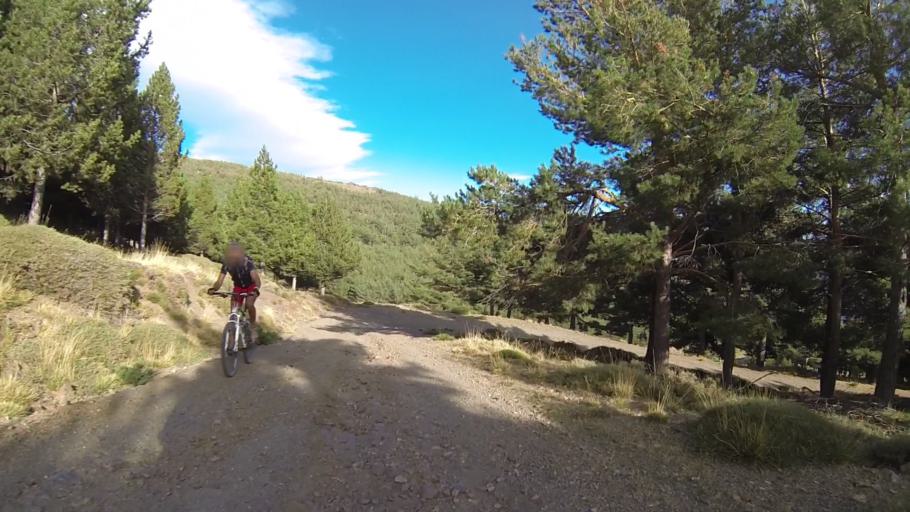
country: ES
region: Andalusia
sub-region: Provincia de Almeria
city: Paterna del Rio
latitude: 37.0819
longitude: -2.9024
